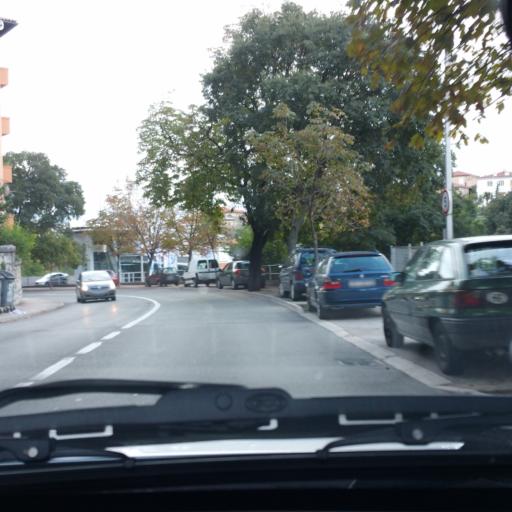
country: HR
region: Primorsko-Goranska
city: Drenova
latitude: 45.3390
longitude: 14.4292
